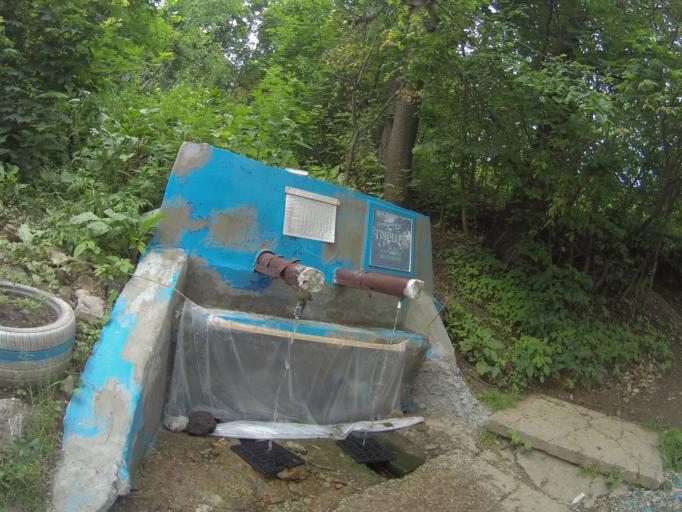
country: RU
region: Vladimir
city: Vladimir
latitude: 56.1234
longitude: 40.3891
